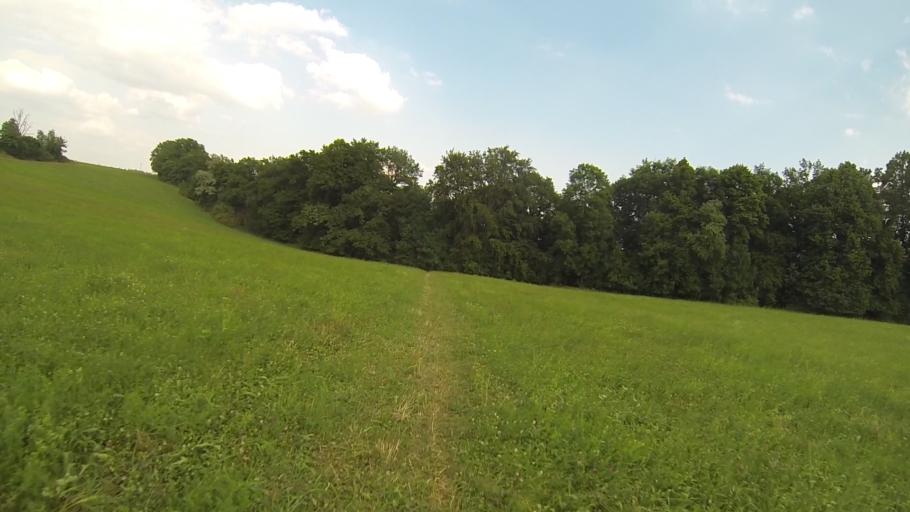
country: DE
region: Baden-Wuerttemberg
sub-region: Tuebingen Region
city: Blaubeuren
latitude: 48.4514
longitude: 9.8557
